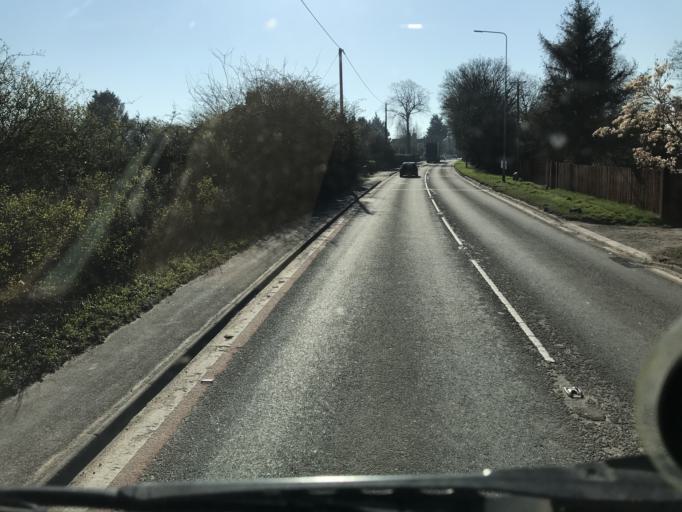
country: GB
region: England
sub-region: Cheshire West and Chester
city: Waverton
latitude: 53.1771
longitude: -2.8279
